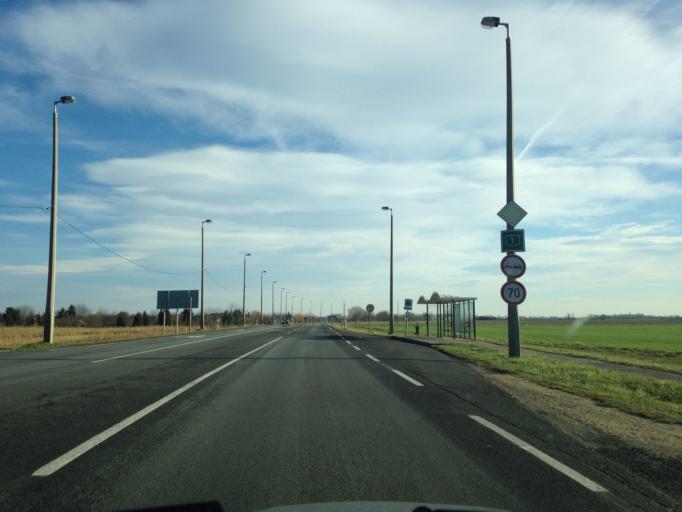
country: HU
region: Gyor-Moson-Sopron
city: Kimle
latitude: 47.8128
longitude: 17.3558
